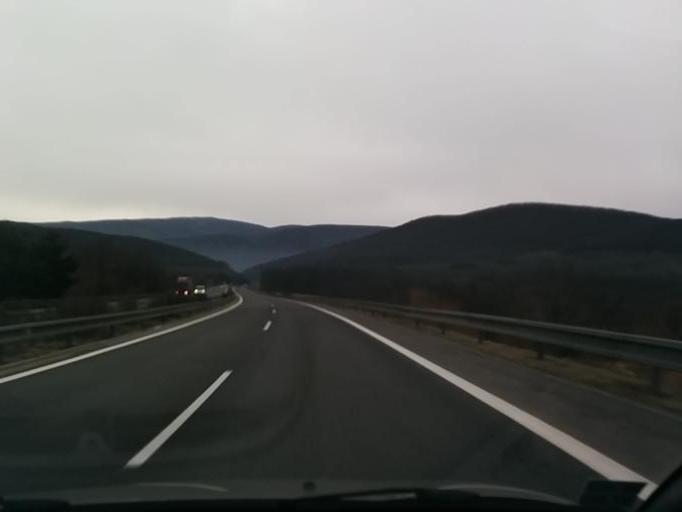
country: SK
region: Nitriansky
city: Tlmace
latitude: 48.3668
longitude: 18.5476
